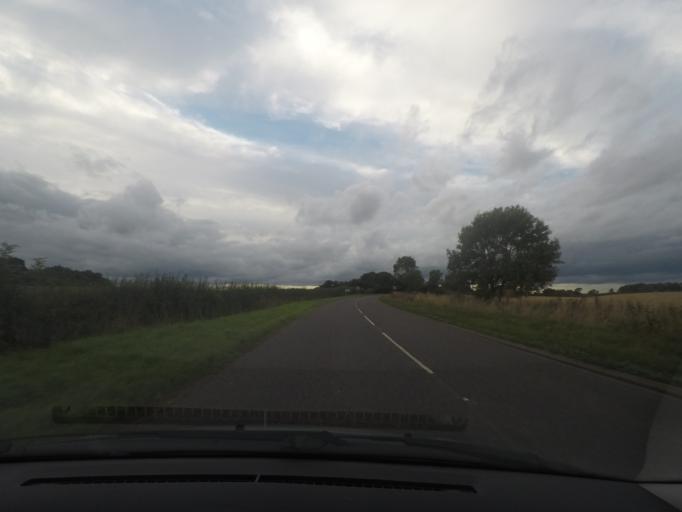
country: GB
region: England
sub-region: Lincolnshire
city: Burwell
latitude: 53.2653
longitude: 0.0816
